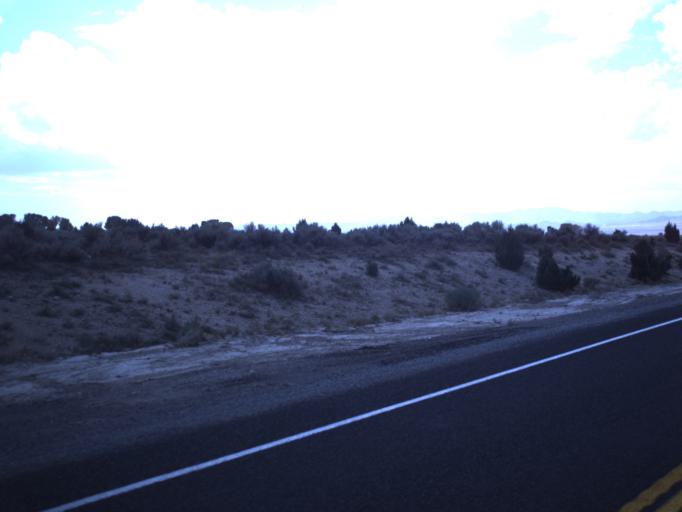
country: US
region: Utah
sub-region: Utah County
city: Eagle Mountain
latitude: 40.2315
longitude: -112.1782
